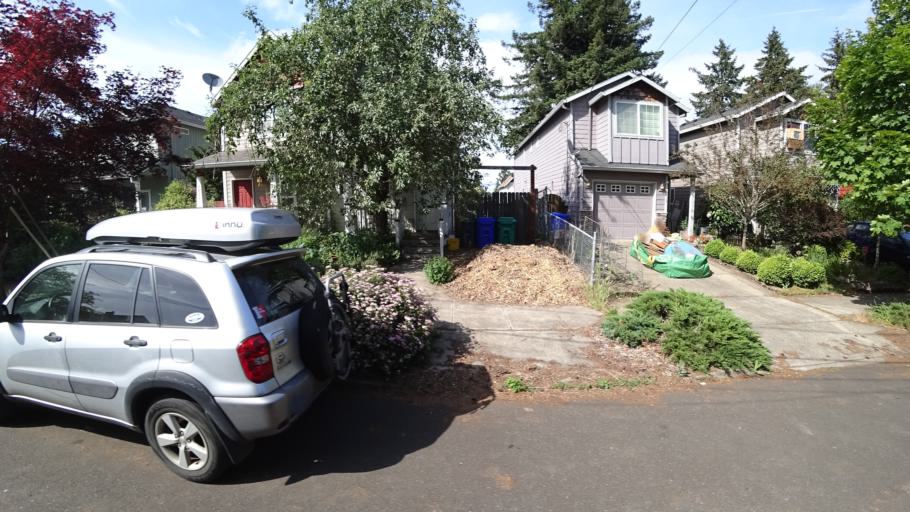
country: US
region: Oregon
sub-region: Washington County
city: West Haven
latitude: 45.5917
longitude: -122.7337
